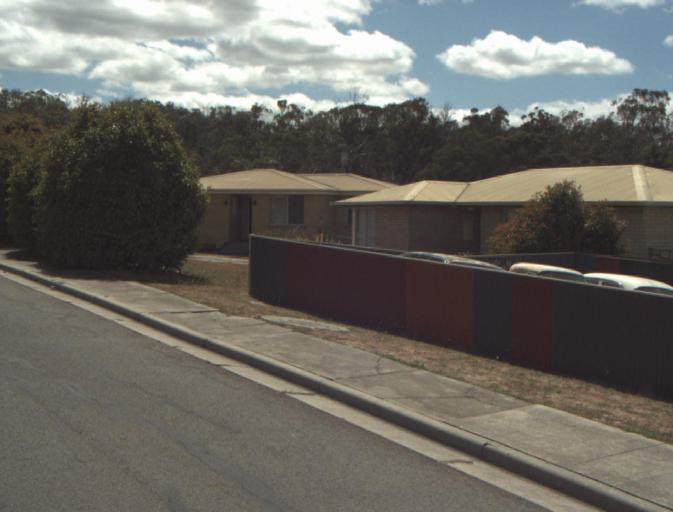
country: AU
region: Tasmania
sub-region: Launceston
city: Newstead
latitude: -41.4095
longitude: 147.1690
